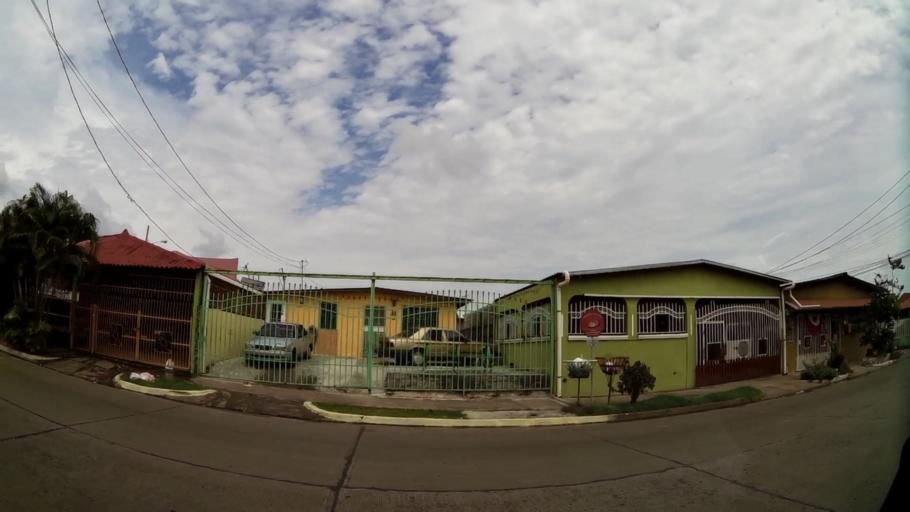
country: PA
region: Panama
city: Tocumen
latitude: 9.0501
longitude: -79.4139
